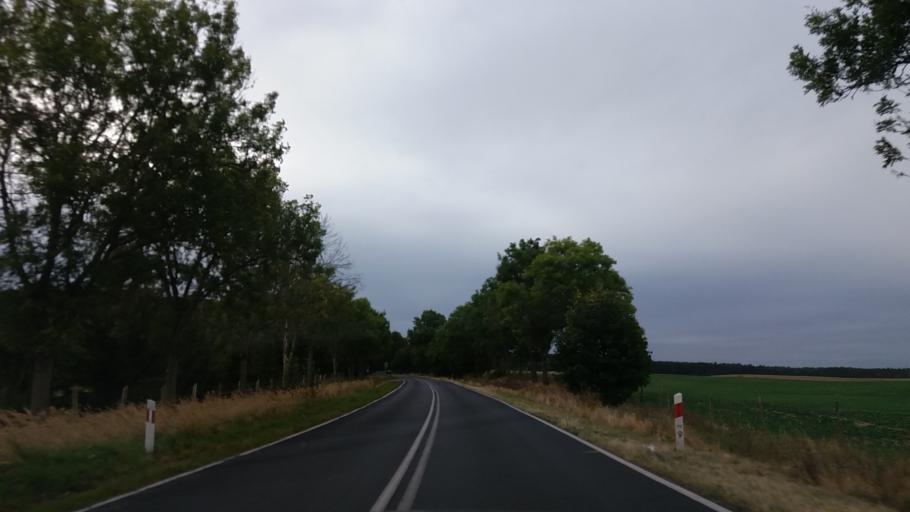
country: PL
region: West Pomeranian Voivodeship
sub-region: Powiat mysliborski
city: Barlinek
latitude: 52.9579
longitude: 15.1822
